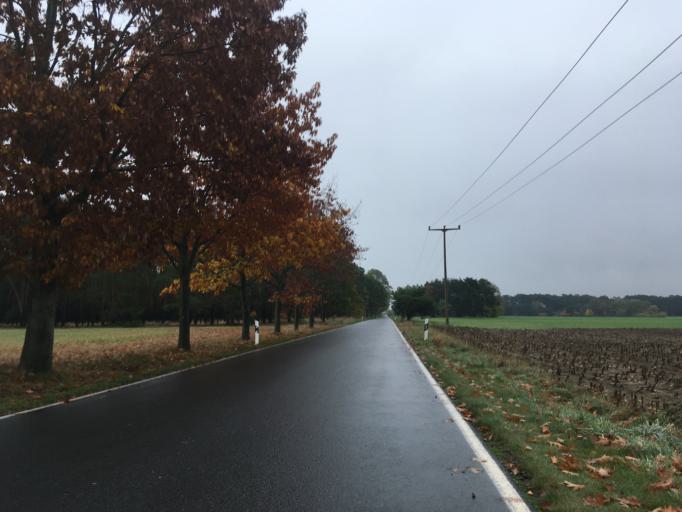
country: DE
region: Brandenburg
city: Neu Zauche
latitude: 52.0157
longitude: 14.1567
